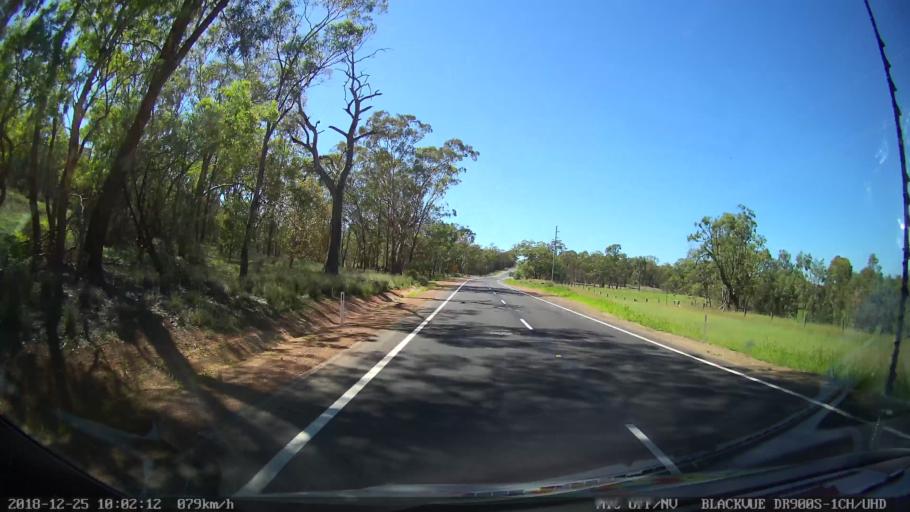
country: AU
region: New South Wales
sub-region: Upper Hunter Shire
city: Merriwa
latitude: -32.2159
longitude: 150.4622
